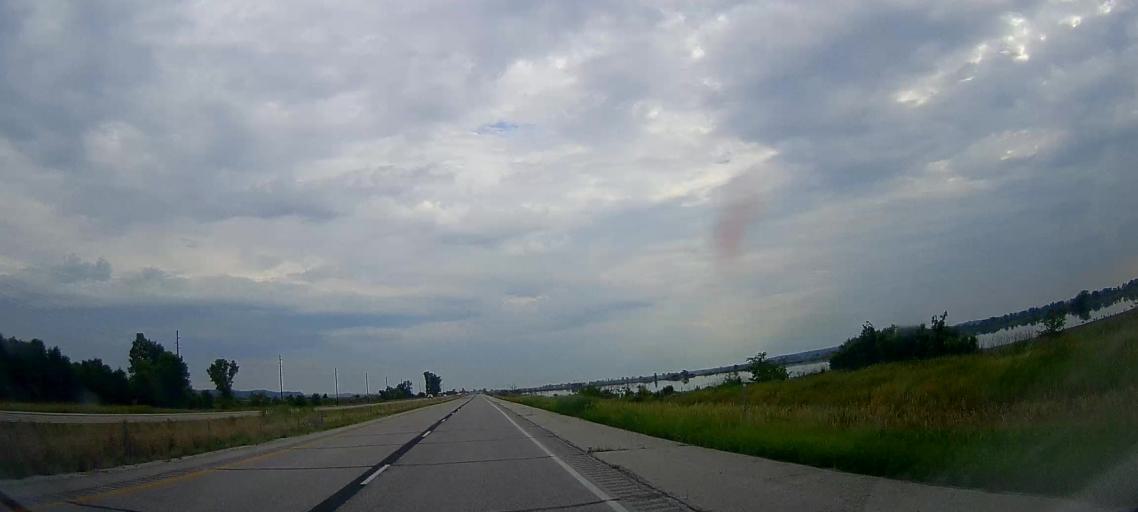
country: US
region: Iowa
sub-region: Harrison County
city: Missouri Valley
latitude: 41.4639
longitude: -95.8997
